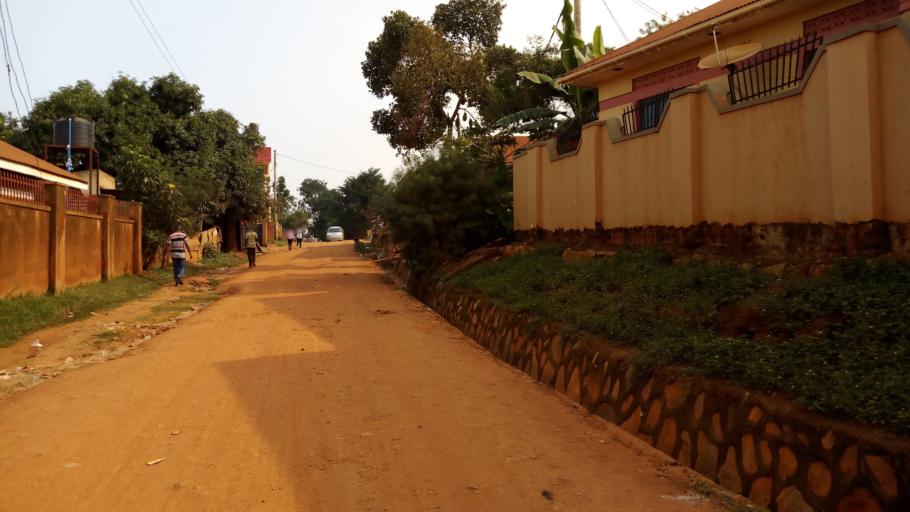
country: UG
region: Central Region
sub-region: Wakiso District
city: Kireka
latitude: 0.3110
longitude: 32.6500
